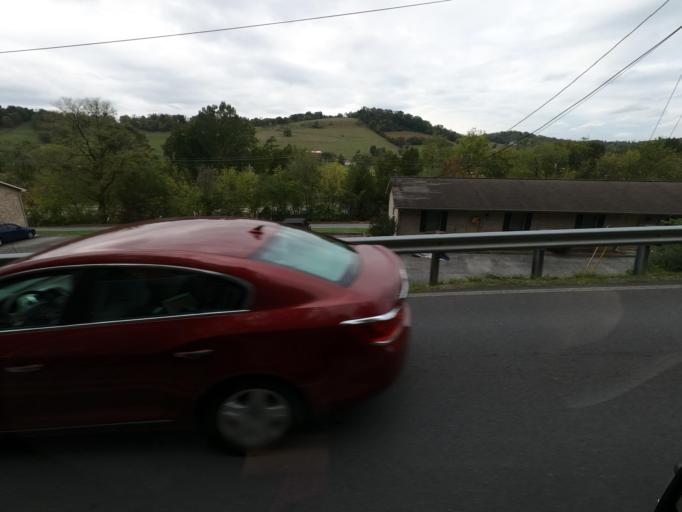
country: US
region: Tennessee
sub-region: Carter County
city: Central
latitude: 36.3393
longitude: -82.2565
